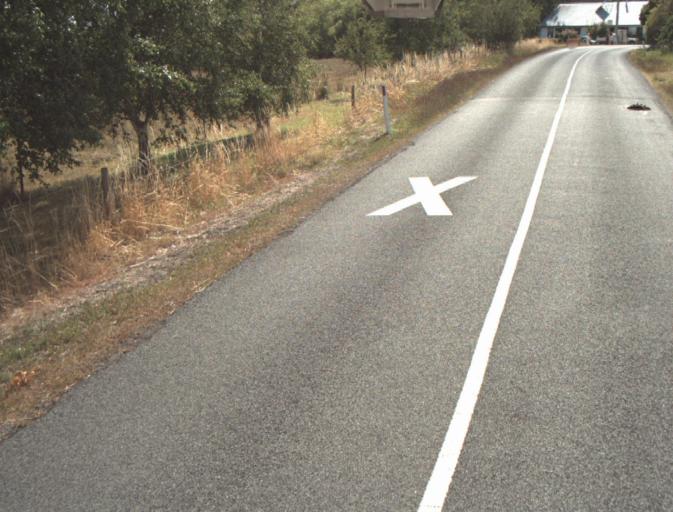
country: AU
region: Tasmania
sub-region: Launceston
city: Mayfield
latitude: -41.2597
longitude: 147.1777
